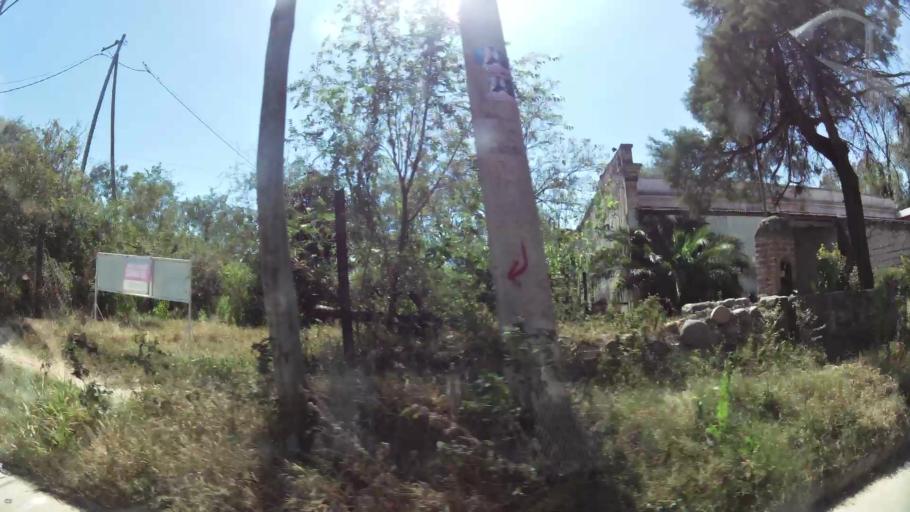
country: AR
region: Cordoba
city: Saldan
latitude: -31.3371
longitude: -64.2831
